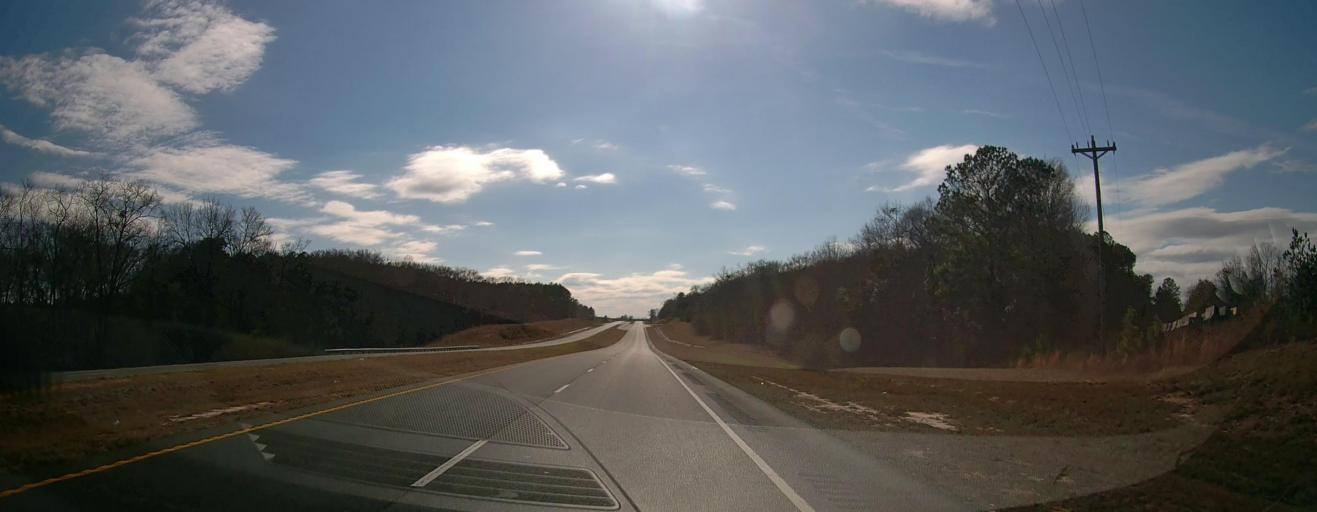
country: US
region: Georgia
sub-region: Taylor County
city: Butler
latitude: 32.4307
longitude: -84.2808
